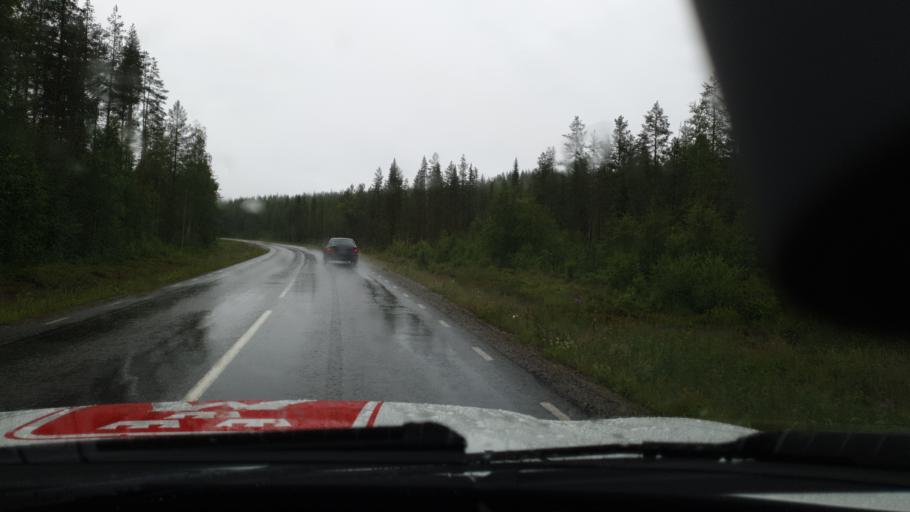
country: SE
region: Vaesterbotten
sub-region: Norsjo Kommun
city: Norsjoe
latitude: 64.8656
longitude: 19.7269
